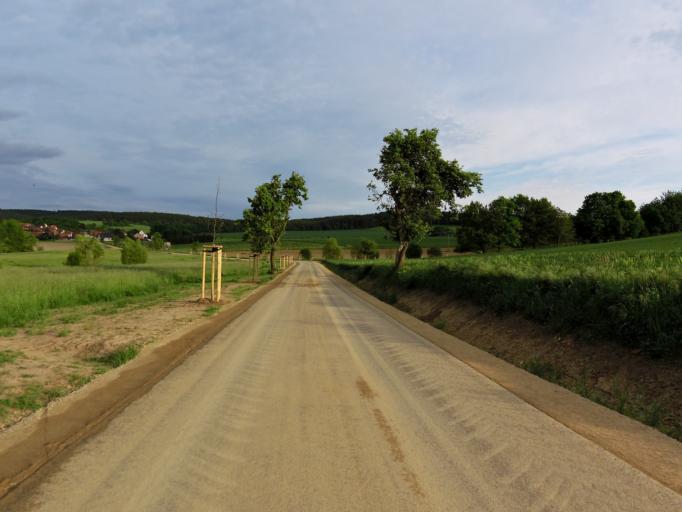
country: DE
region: Thuringia
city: Dippach
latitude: 50.9123
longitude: 10.0915
